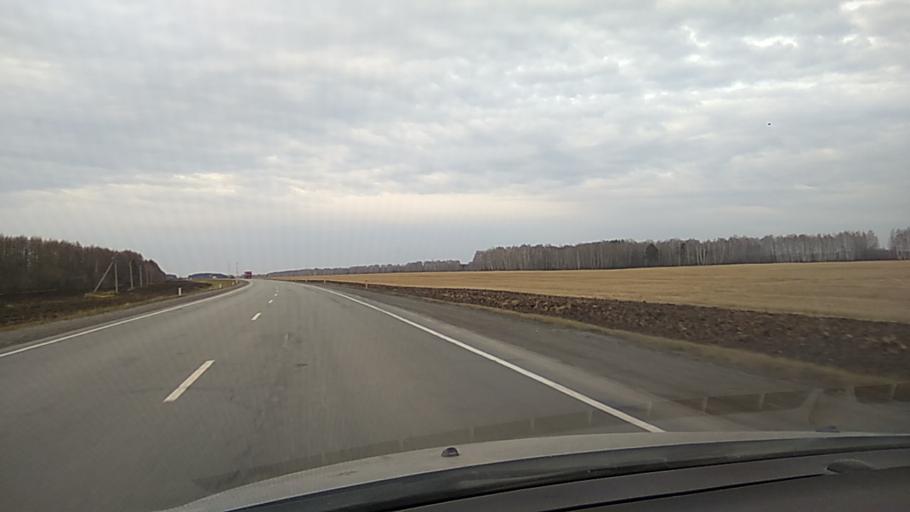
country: RU
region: Sverdlovsk
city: Troitskiy
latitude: 57.0915
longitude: 63.8008
